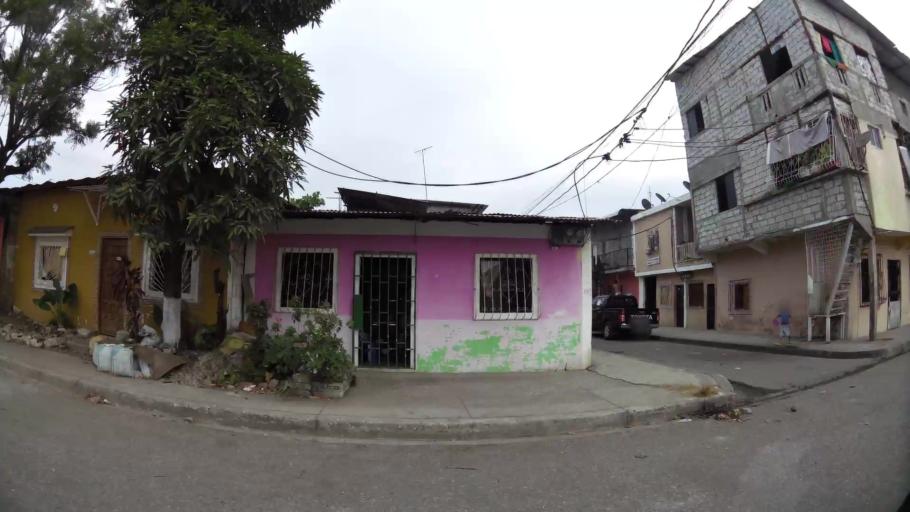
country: EC
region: Guayas
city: Guayaquil
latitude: -2.2626
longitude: -79.8817
